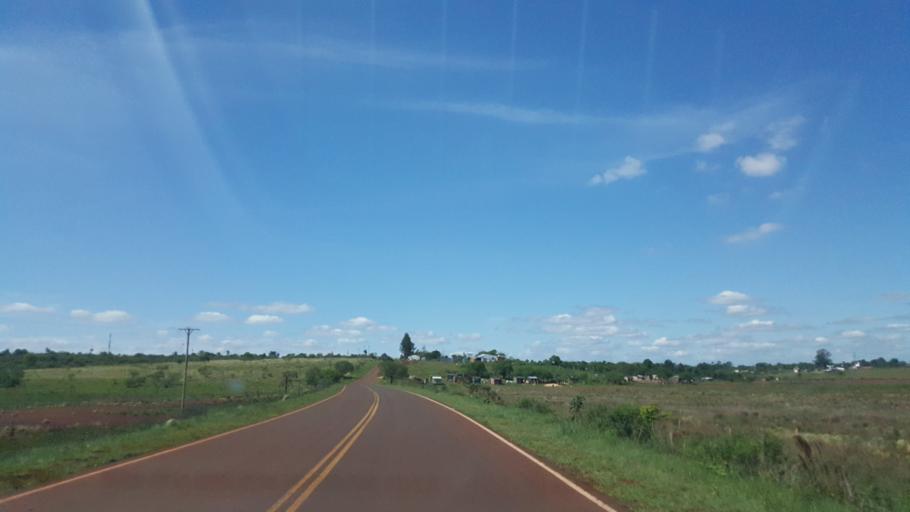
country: AR
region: Misiones
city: Garupa
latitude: -27.4921
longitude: -55.8366
